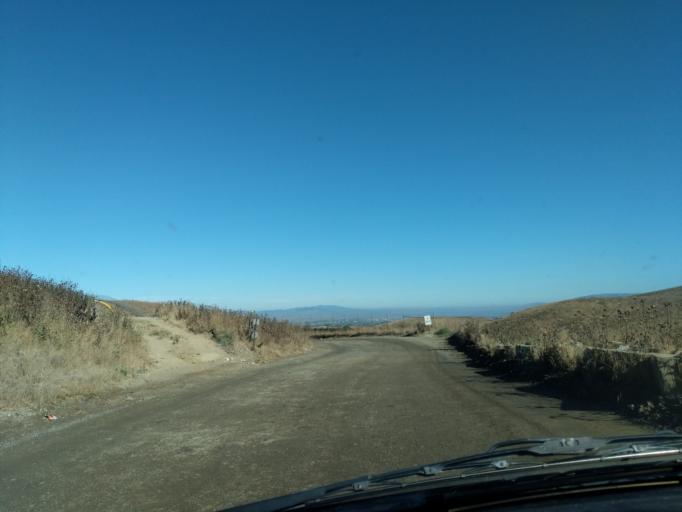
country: US
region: California
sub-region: San Benito County
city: Ridgemark
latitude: 36.8265
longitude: -121.3229
